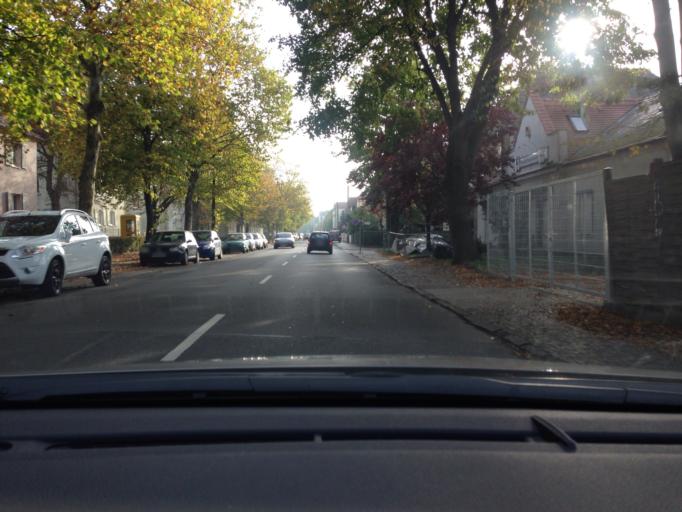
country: DE
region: Saxony
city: Taucha
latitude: 51.3815
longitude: 12.4837
